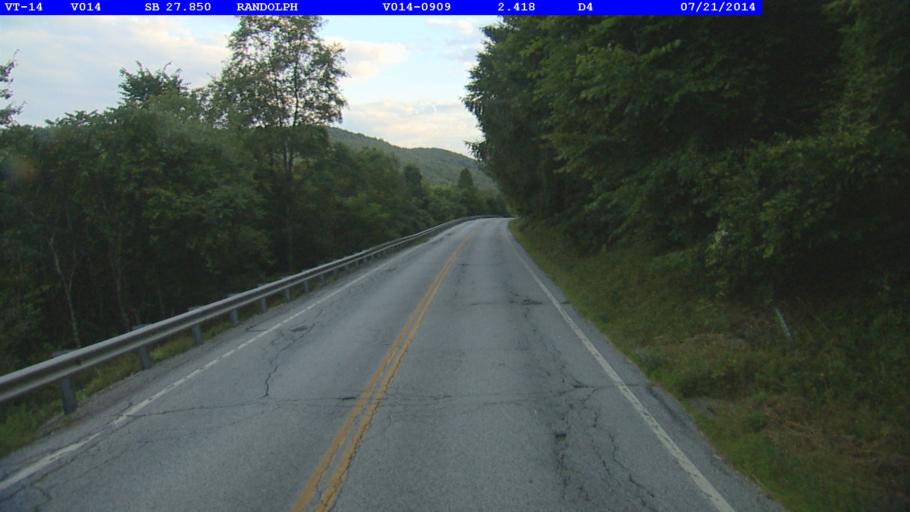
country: US
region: Vermont
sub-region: Orange County
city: Randolph
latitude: 43.9057
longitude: -72.5631
